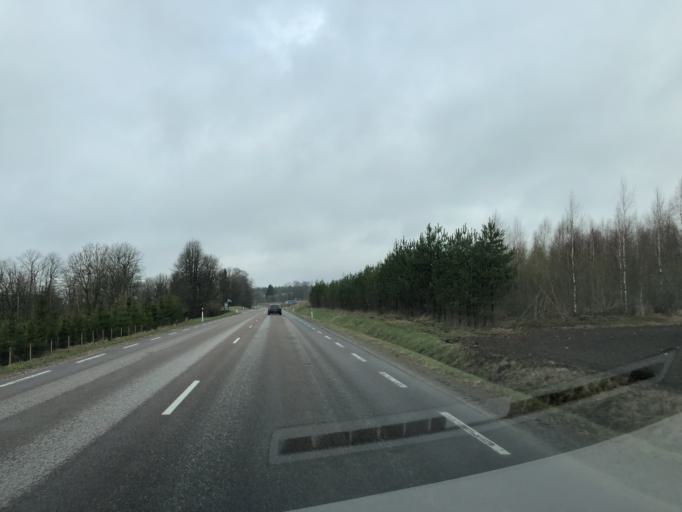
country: EE
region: Jogevamaa
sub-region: Jogeva linn
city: Jogeva
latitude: 58.6872
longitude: 26.4645
